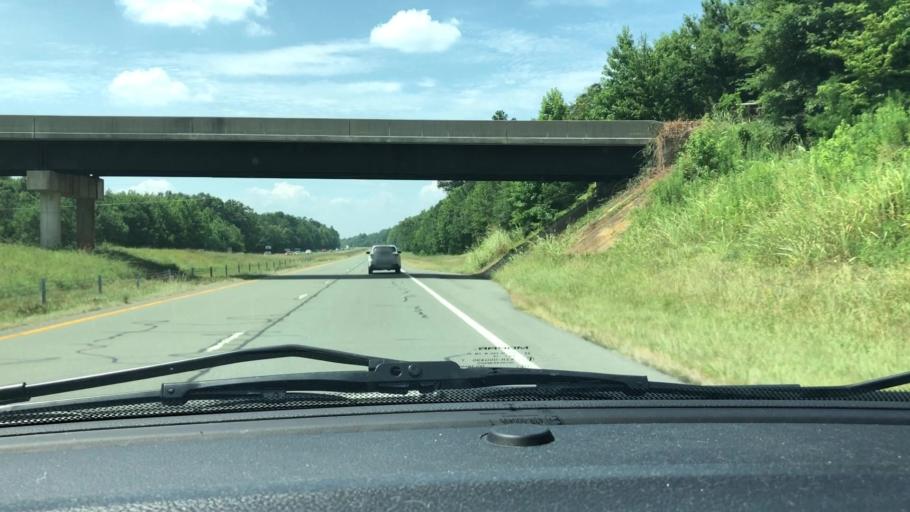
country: US
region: North Carolina
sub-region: Randolph County
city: Liberty
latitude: 35.8025
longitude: -79.5397
